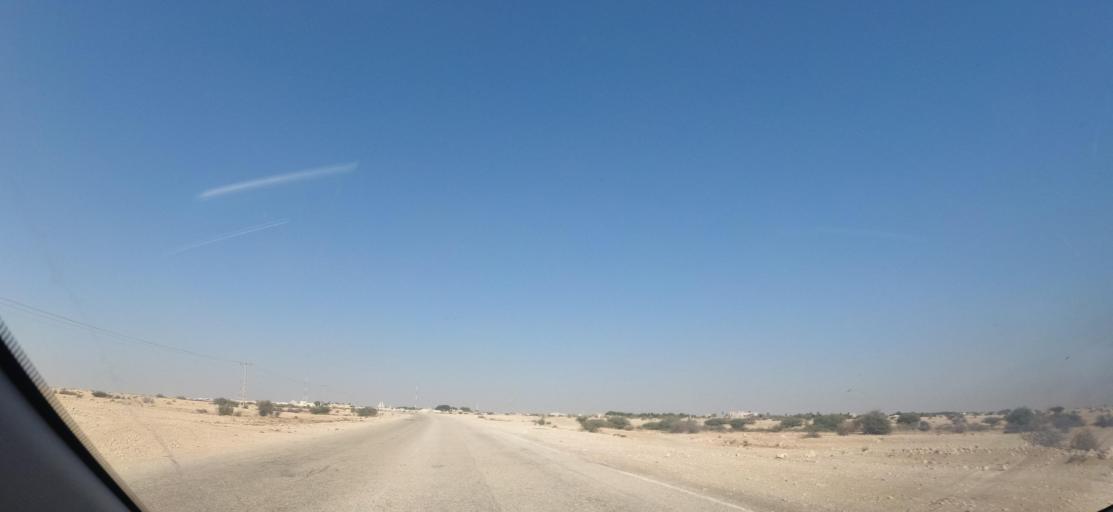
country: QA
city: Al Jumayliyah
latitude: 25.6070
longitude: 51.0764
